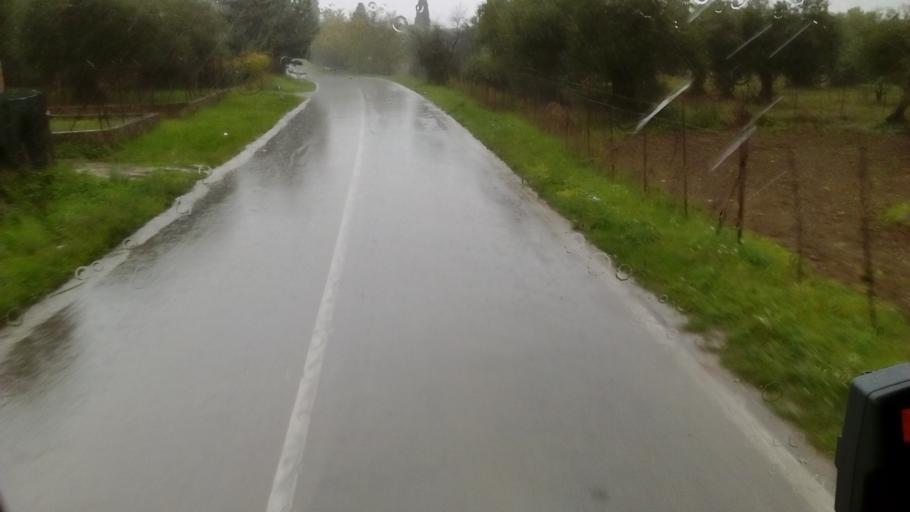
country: IT
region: Sicily
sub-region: Enna
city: Pietraperzia
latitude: 37.4211
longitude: 14.1632
